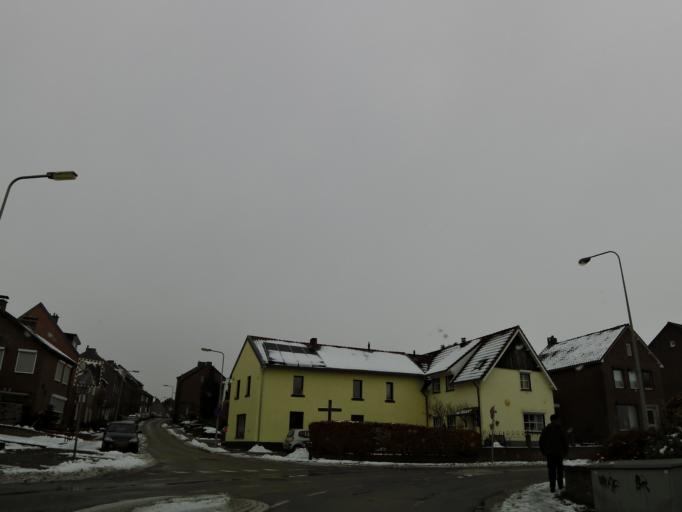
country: NL
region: Limburg
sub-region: Gemeente Simpelveld
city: Simpelveld
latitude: 50.8206
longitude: 6.0108
